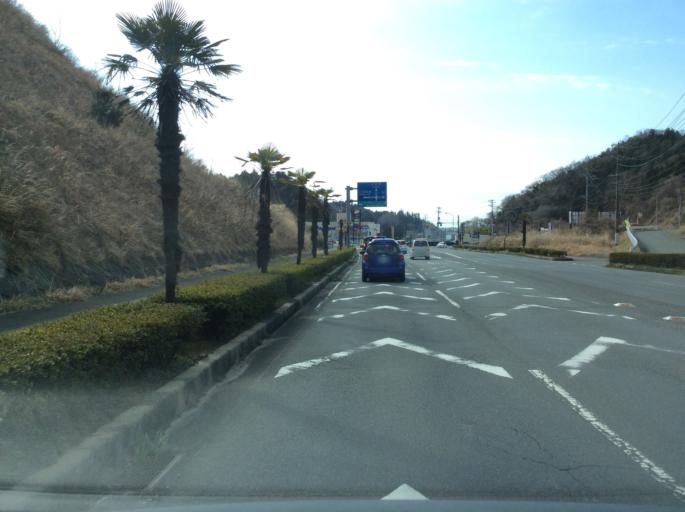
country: JP
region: Fukushima
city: Iwaki
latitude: 36.9747
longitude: 140.9045
